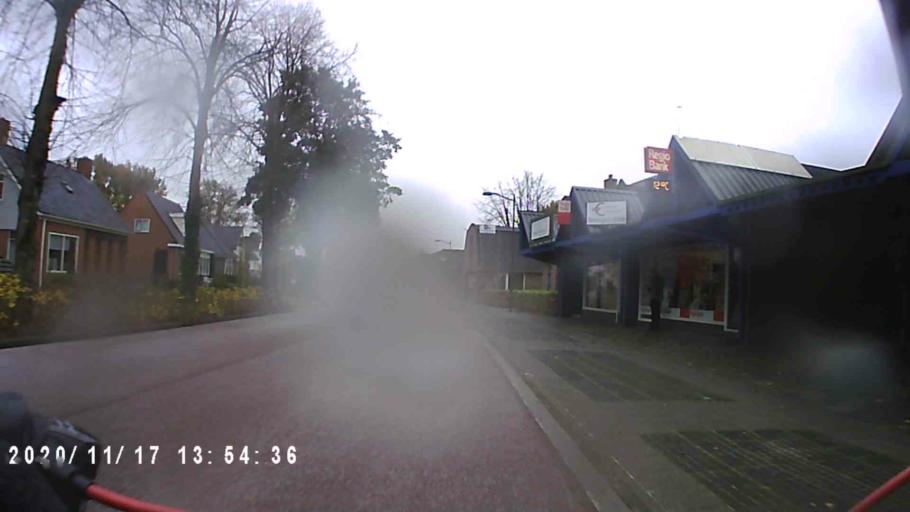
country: NL
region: Groningen
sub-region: Gemeente Zuidhorn
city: Zuidhorn
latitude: 53.2252
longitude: 6.3534
